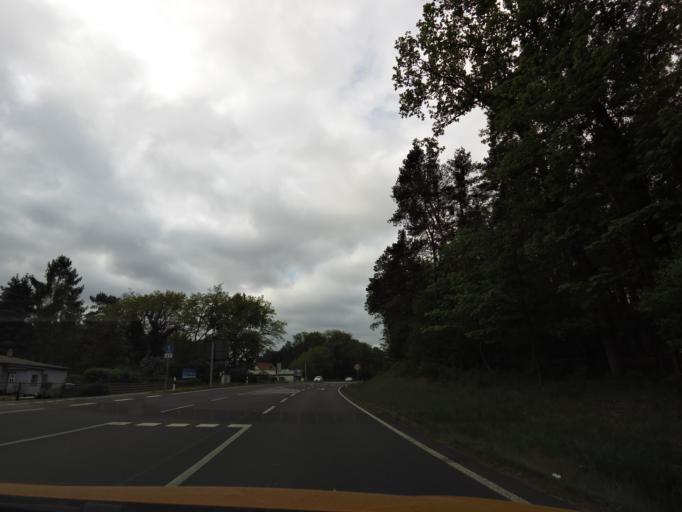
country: DE
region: Brandenburg
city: Michendorf
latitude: 52.2963
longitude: 13.0245
